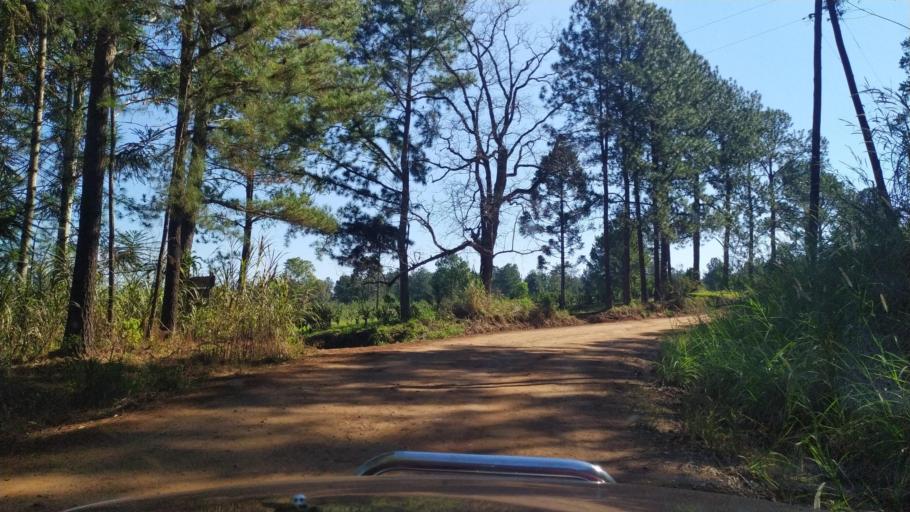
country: AR
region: Misiones
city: El Alcazar
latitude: -26.7235
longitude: -54.6855
